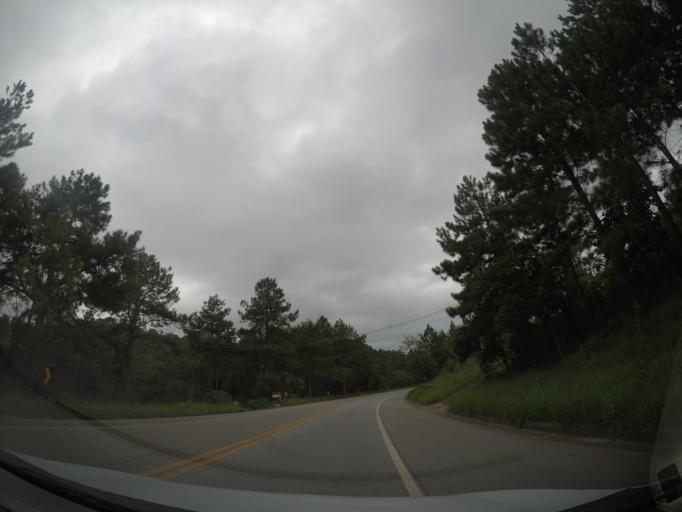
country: BR
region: Sao Paulo
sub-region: Aruja
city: Aruja
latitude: -23.3572
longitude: -46.4209
